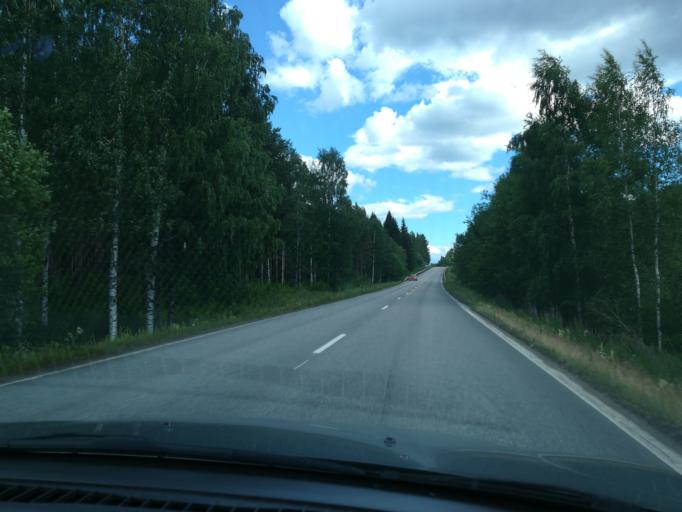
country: FI
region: Southern Savonia
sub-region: Mikkeli
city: Hirvensalmi
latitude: 61.6707
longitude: 26.7715
